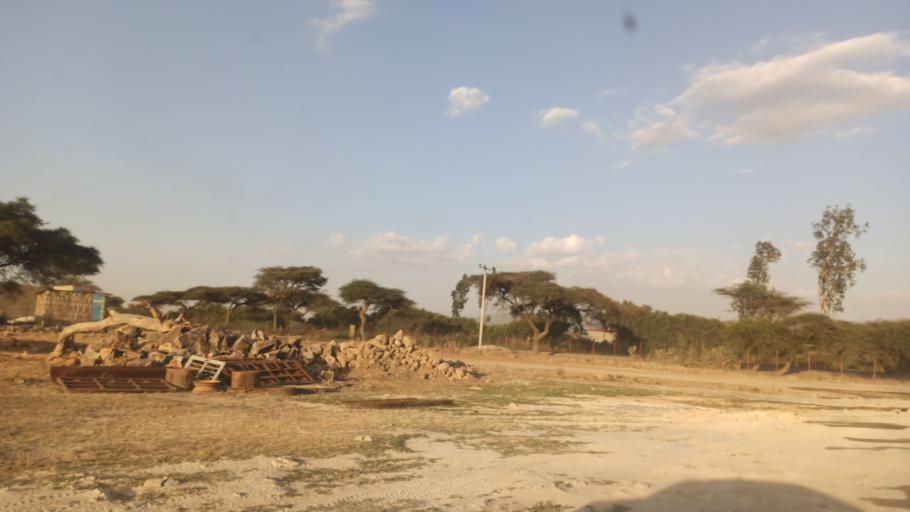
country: ET
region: Oromiya
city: Ziway
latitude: 7.6988
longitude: 38.6564
